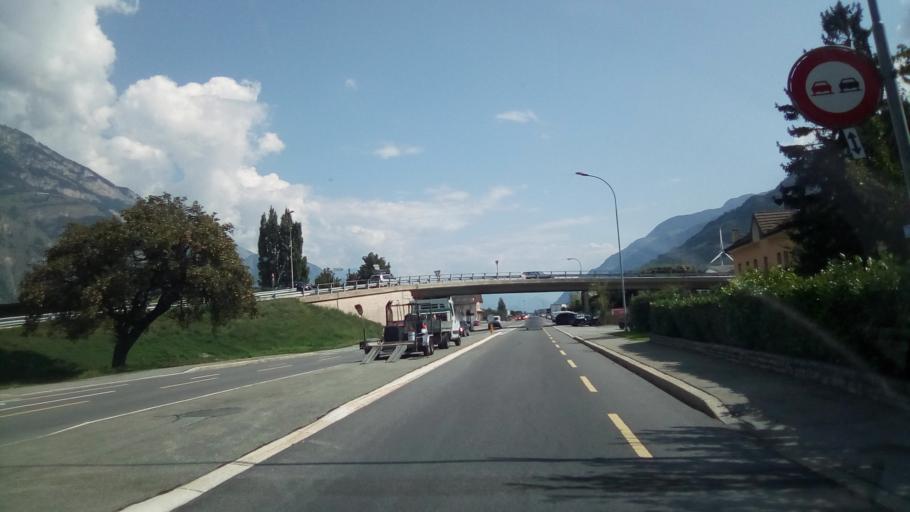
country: CH
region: Valais
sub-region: Martigny District
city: Charrat-les-Chenes
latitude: 46.1264
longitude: 7.1271
